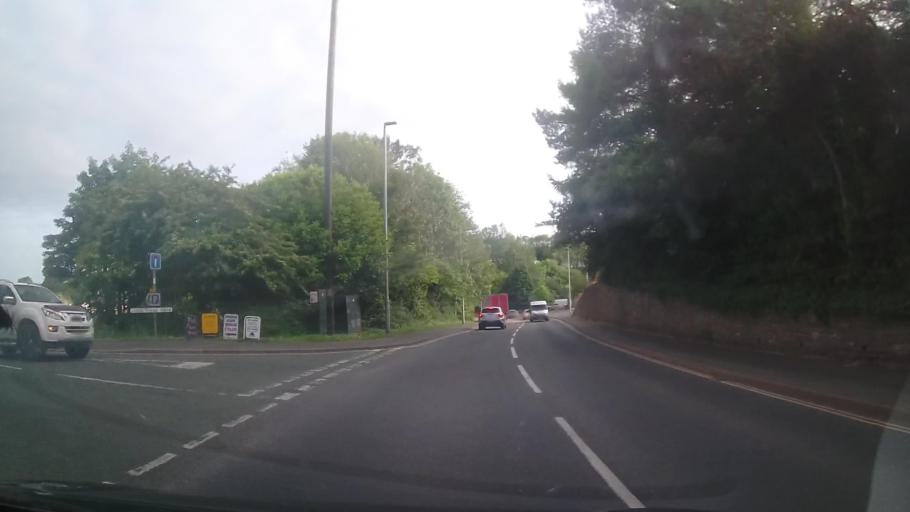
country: GB
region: England
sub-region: Devon
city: Kingsbridge
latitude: 50.2855
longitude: -3.7802
